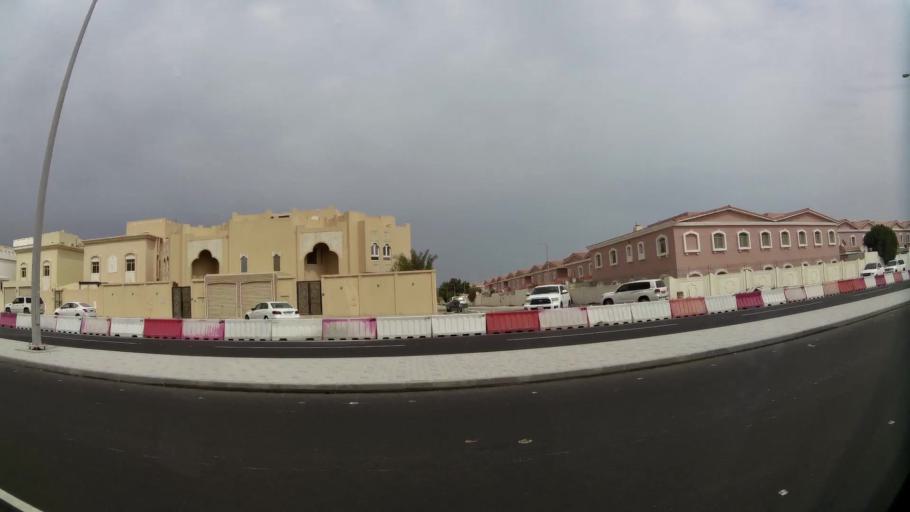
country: QA
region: Baladiyat ar Rayyan
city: Ar Rayyan
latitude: 25.3523
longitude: 51.4656
